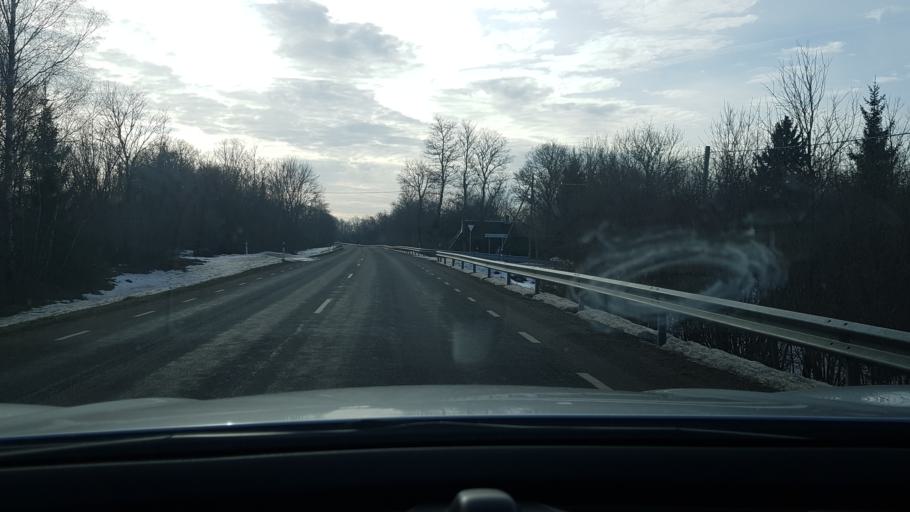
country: EE
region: Saare
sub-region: Kuressaare linn
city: Kuressaare
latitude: 58.3033
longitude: 22.5392
